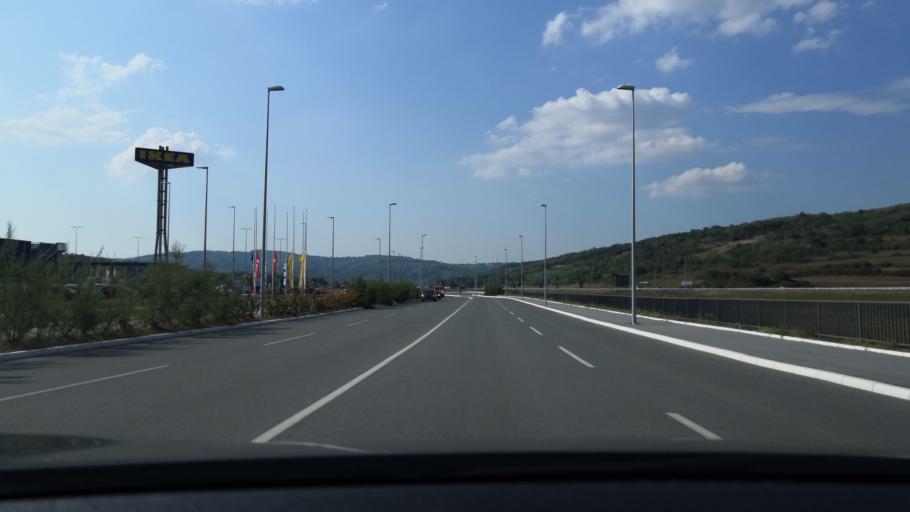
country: RS
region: Central Serbia
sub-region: Belgrade
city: Zvezdara
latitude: 44.7108
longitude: 20.5646
